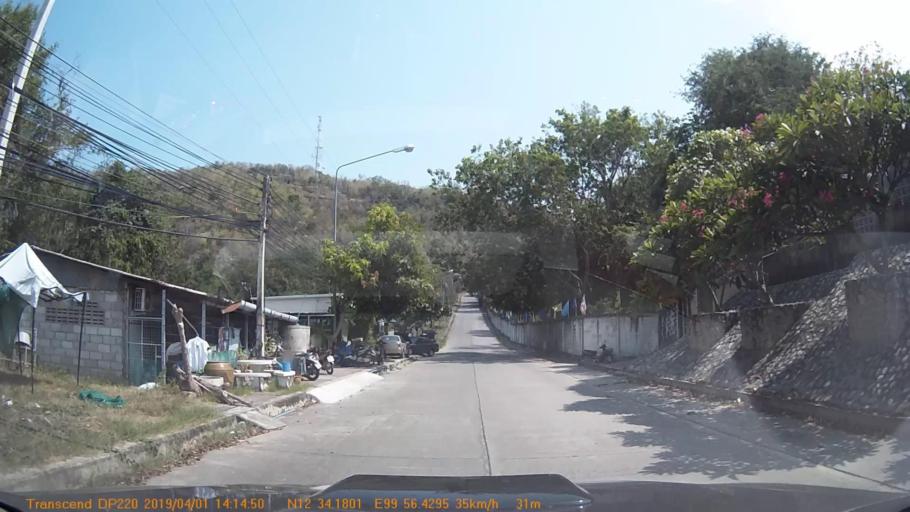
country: TH
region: Prachuap Khiri Khan
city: Hua Hin
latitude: 12.5696
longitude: 99.9405
